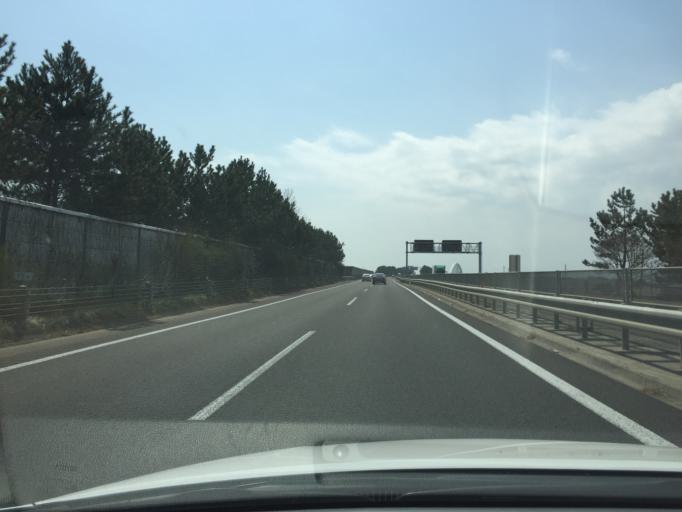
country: JP
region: Miyagi
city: Sendai
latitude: 38.1991
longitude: 140.9423
